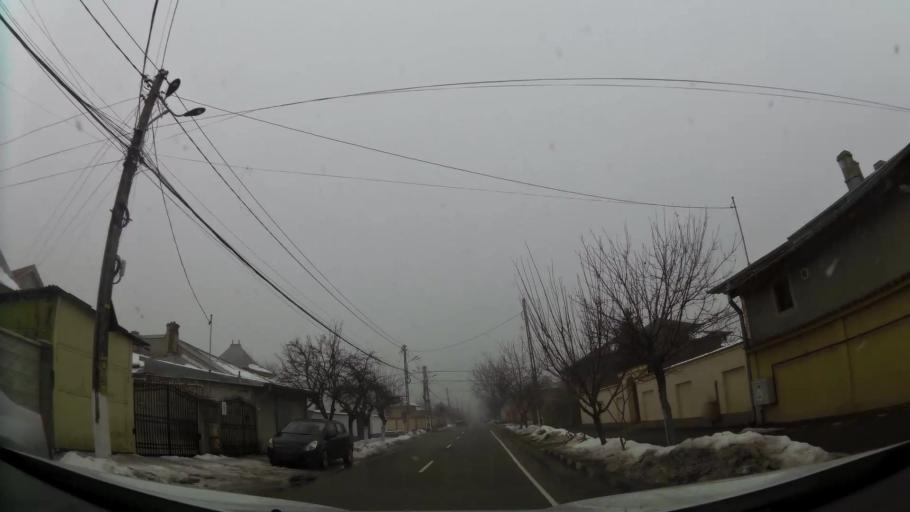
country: RO
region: Ilfov
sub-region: Comuna Chiajna
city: Chiajna
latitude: 44.4583
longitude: 25.9741
